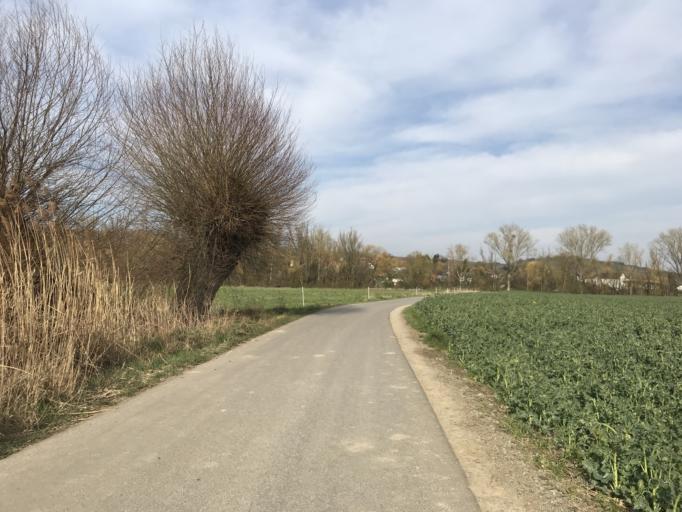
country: DE
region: Rheinland-Pfalz
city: Stadecken-Elsheim
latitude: 49.9139
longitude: 8.1138
